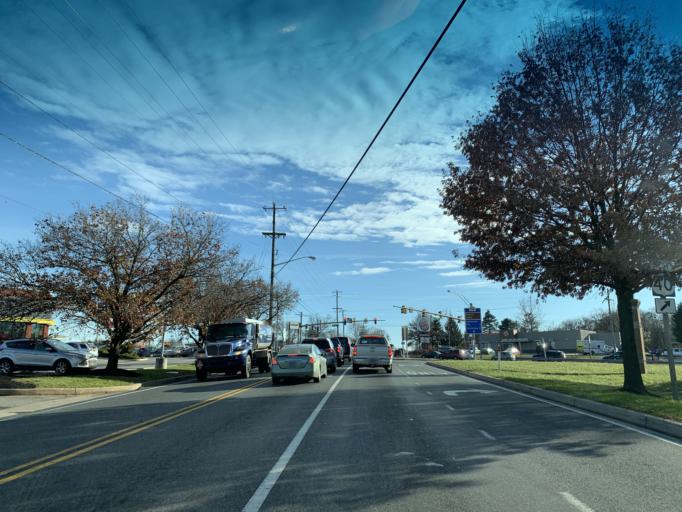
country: US
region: Maryland
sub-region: Cecil County
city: Elkton
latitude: 39.6009
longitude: -75.8281
